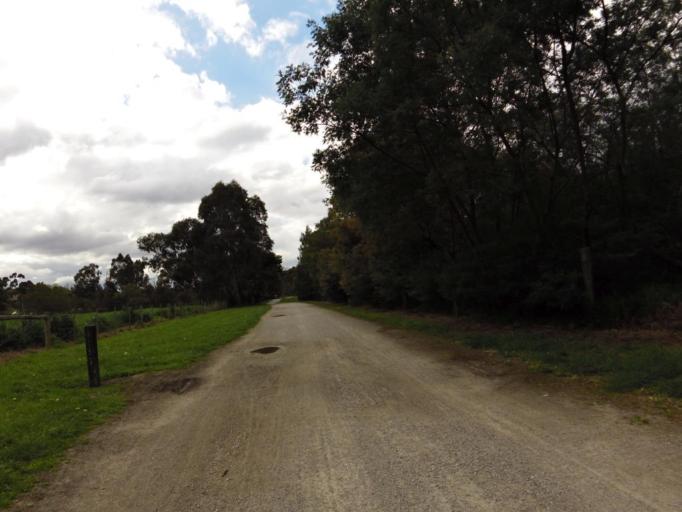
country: AU
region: Victoria
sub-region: Manningham
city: Bulleen
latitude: -37.7648
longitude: 145.0729
